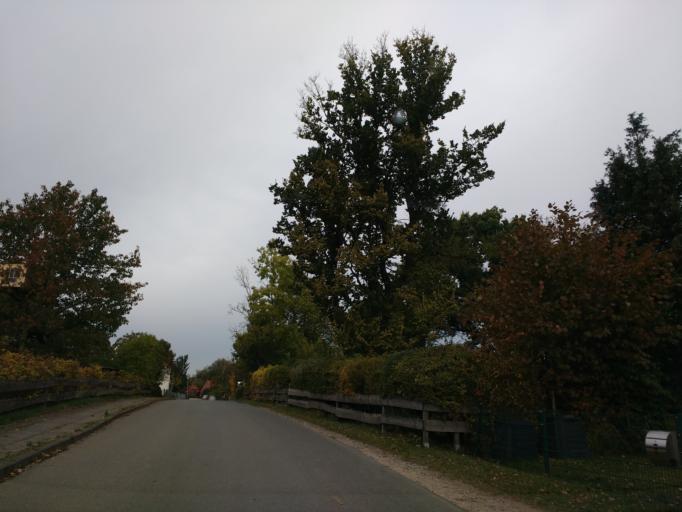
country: DE
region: Schleswig-Holstein
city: Grube
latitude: 54.2033
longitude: 11.0212
